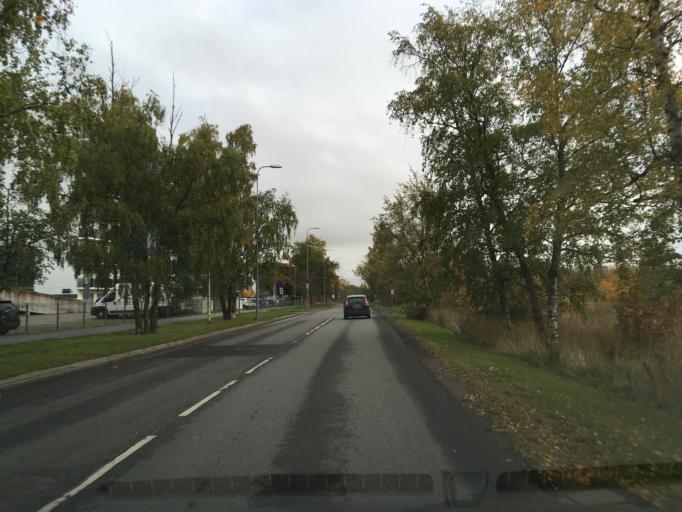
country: EE
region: Harju
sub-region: Viimsi vald
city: Viimsi
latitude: 59.4471
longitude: 24.8245
